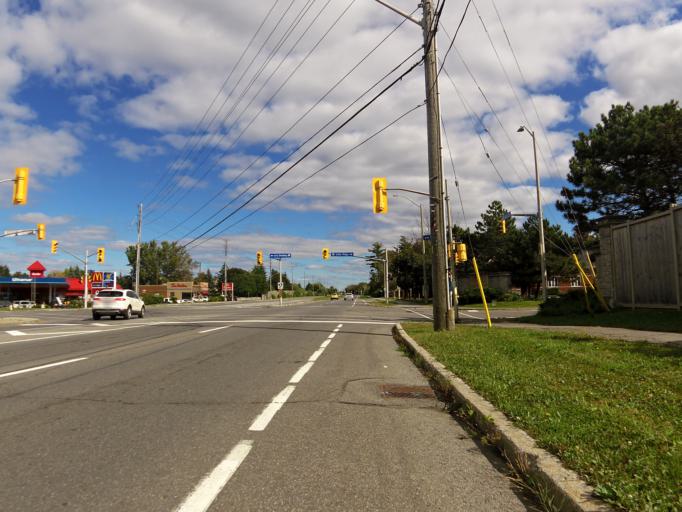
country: CA
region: Ontario
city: Ottawa
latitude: 45.3596
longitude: -75.6320
